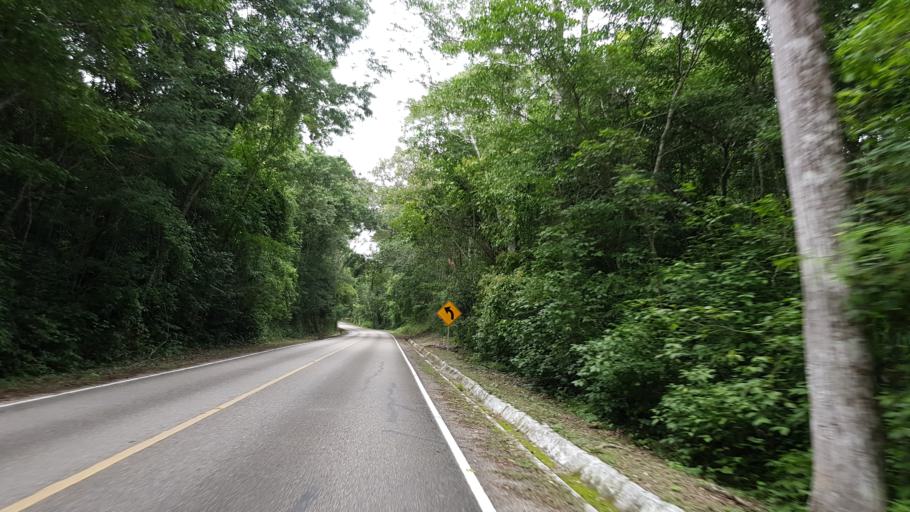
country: GT
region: Peten
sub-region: Municipio de San Jose
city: San Jose
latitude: 17.2170
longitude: -89.6116
